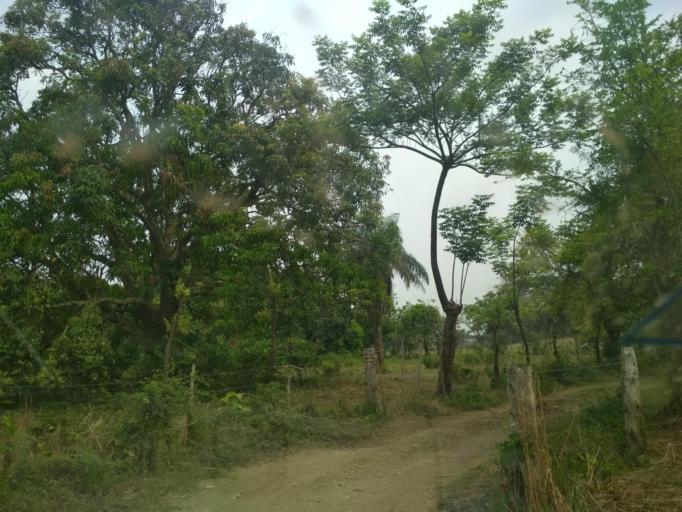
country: MX
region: Veracruz
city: Paso del Toro
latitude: 19.0159
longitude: -96.1479
